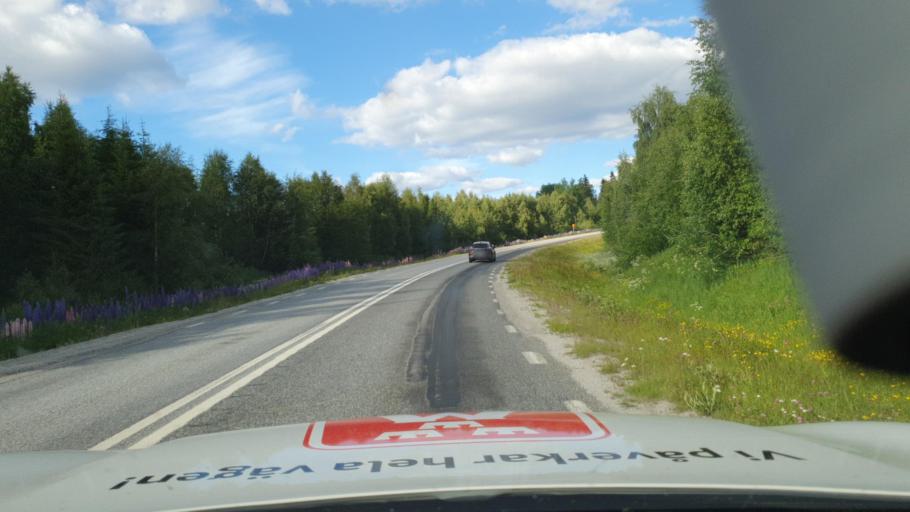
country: SE
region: Vaesterbotten
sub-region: Lycksele Kommun
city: Lycksele
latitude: 64.5179
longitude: 18.3866
